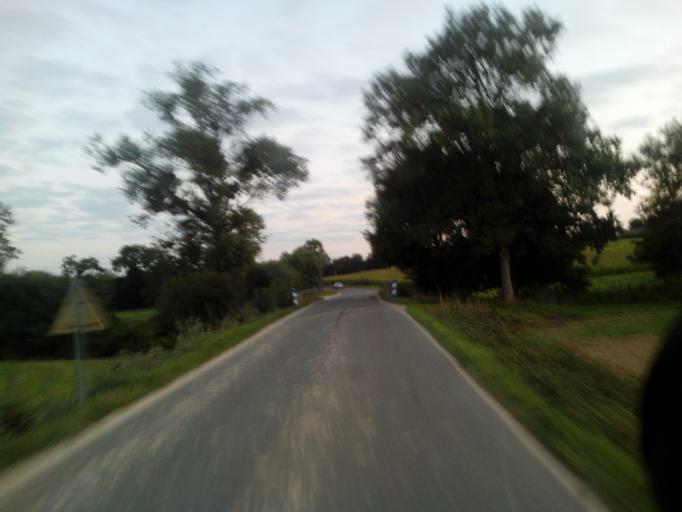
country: FR
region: Brittany
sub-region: Departement d'Ille-et-Vilaine
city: Montfort-sur-Meu
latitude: 48.1520
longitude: -1.9670
